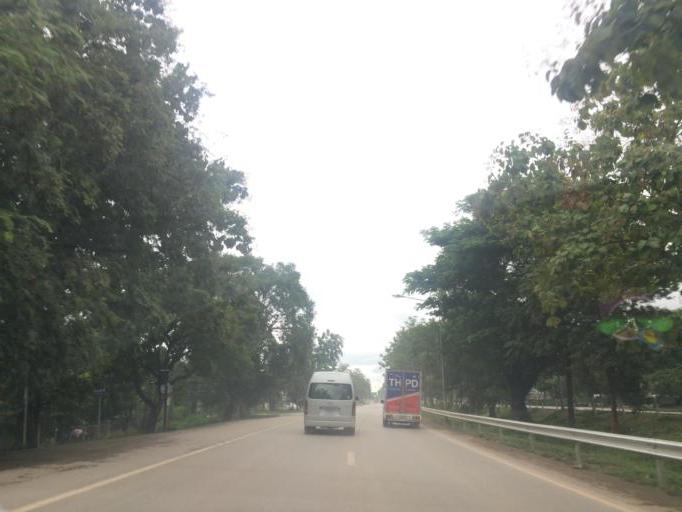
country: TH
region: Chiang Rai
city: Chiang Rai
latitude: 19.8458
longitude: 99.8026
